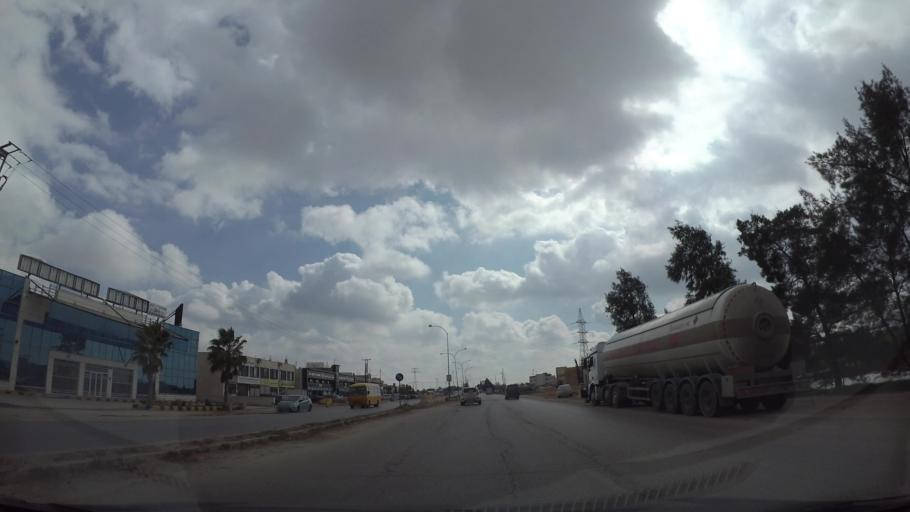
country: JO
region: Amman
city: Jawa
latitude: 31.8197
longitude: 35.9098
